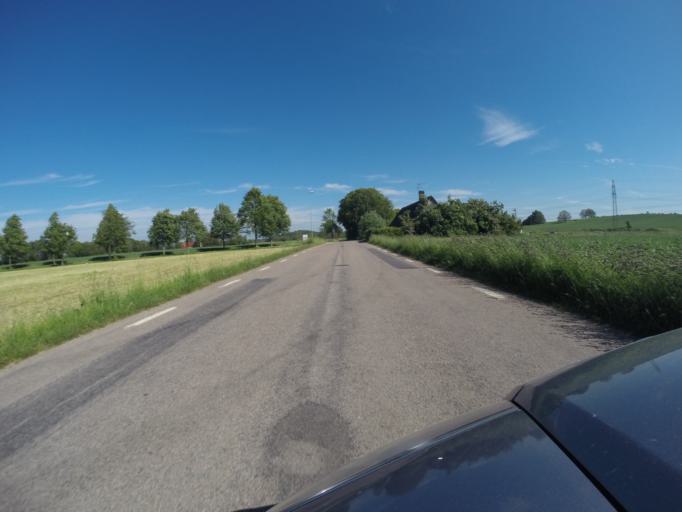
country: SE
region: Skane
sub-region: Helsingborg
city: Morarp
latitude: 56.0738
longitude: 12.8544
